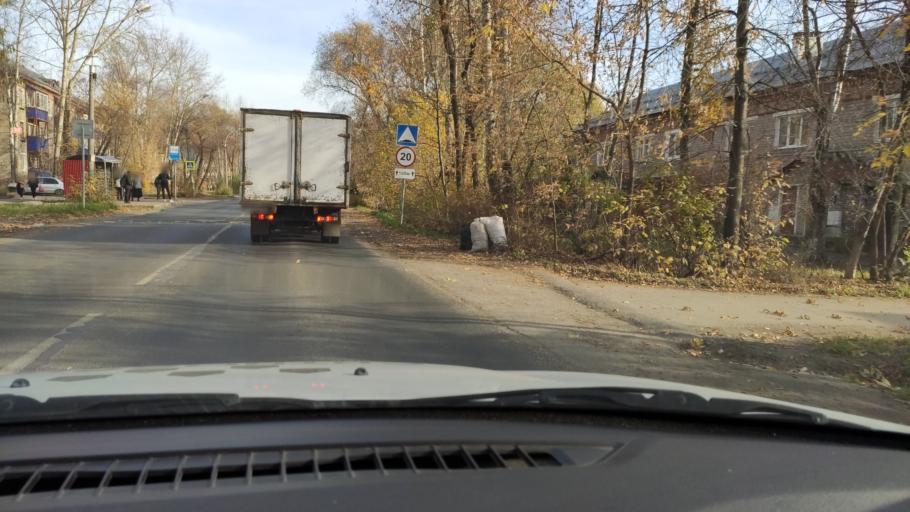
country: RU
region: Perm
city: Perm
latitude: 58.0350
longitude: 56.3540
